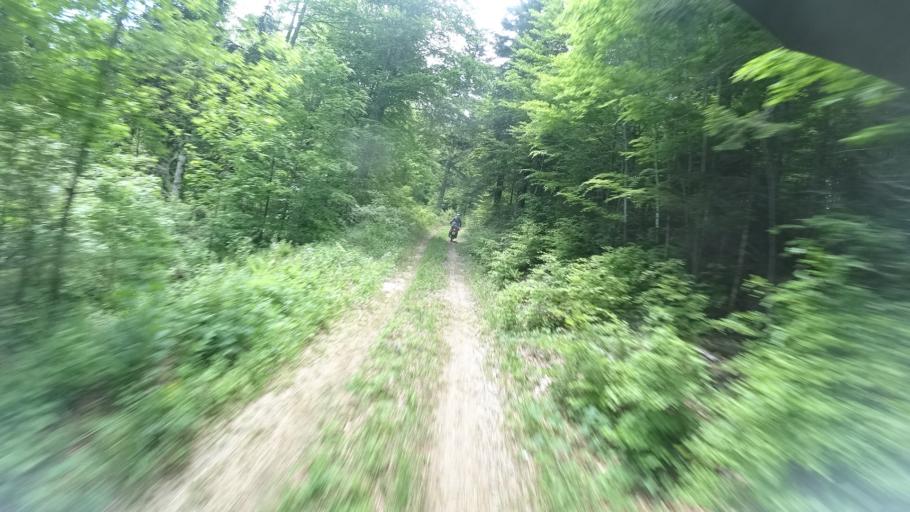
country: HR
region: Zadarska
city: Gracac
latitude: 44.4740
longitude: 15.8917
